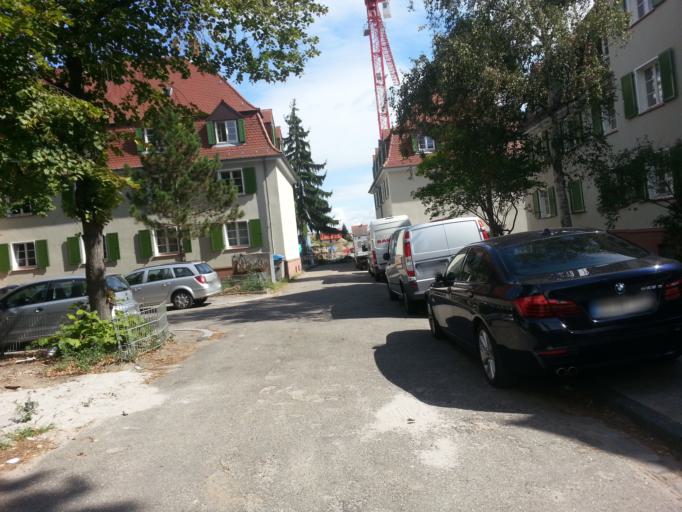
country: DE
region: Baden-Wuerttemberg
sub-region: Karlsruhe Region
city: Mannheim
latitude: 49.5028
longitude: 8.4901
